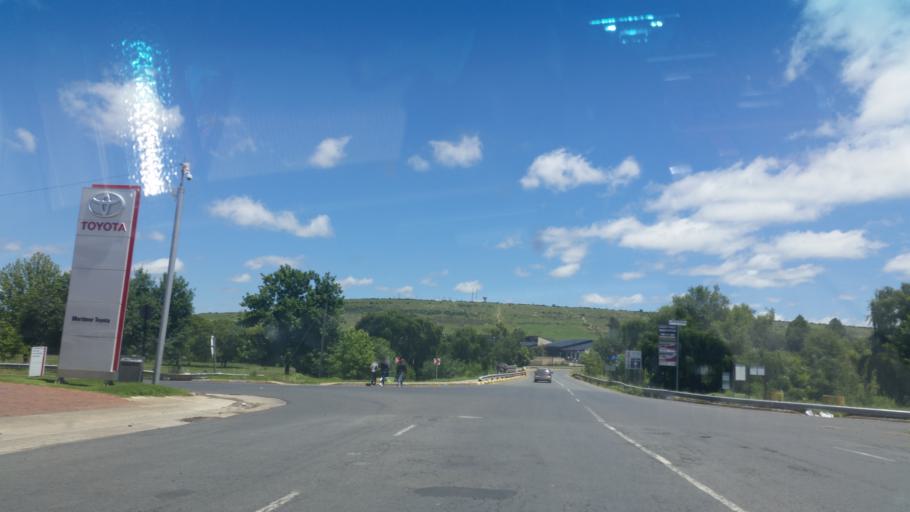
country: ZA
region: Orange Free State
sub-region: Thabo Mofutsanyana District Municipality
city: Harrismith
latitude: -28.2636
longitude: 29.1186
